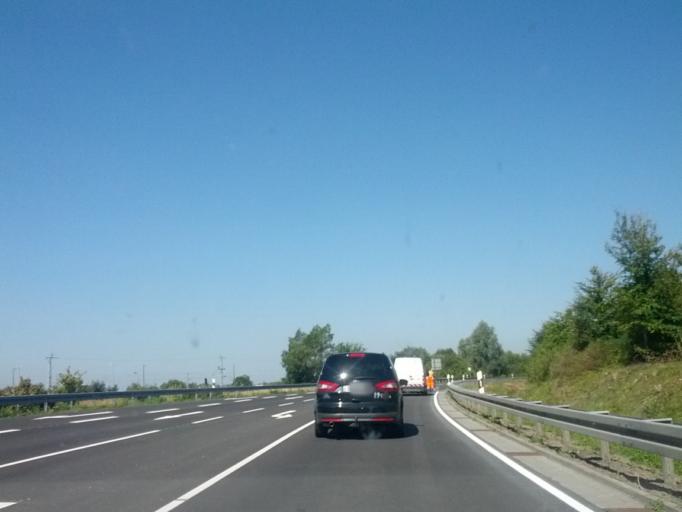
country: DE
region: Mecklenburg-Vorpommern
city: Sagard
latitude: 54.4970
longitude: 13.5657
